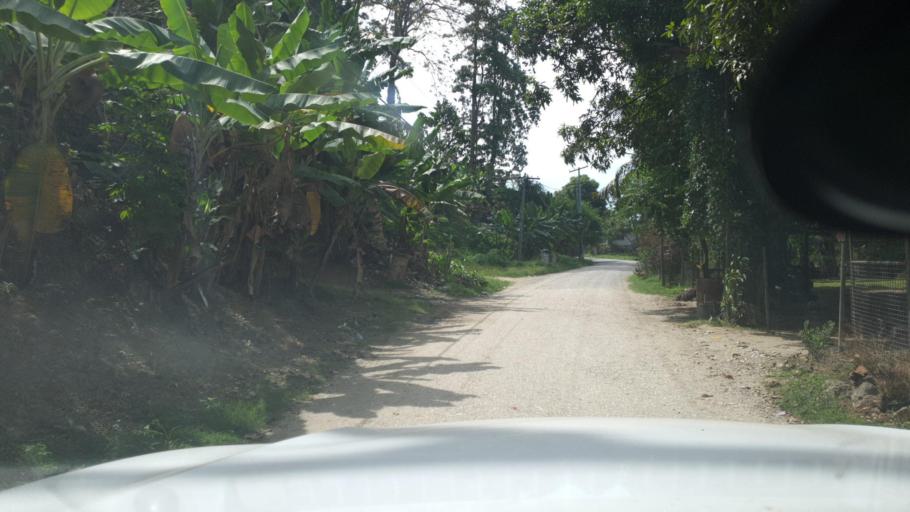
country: SB
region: Guadalcanal
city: Honiara
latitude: -9.4274
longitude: 159.9201
